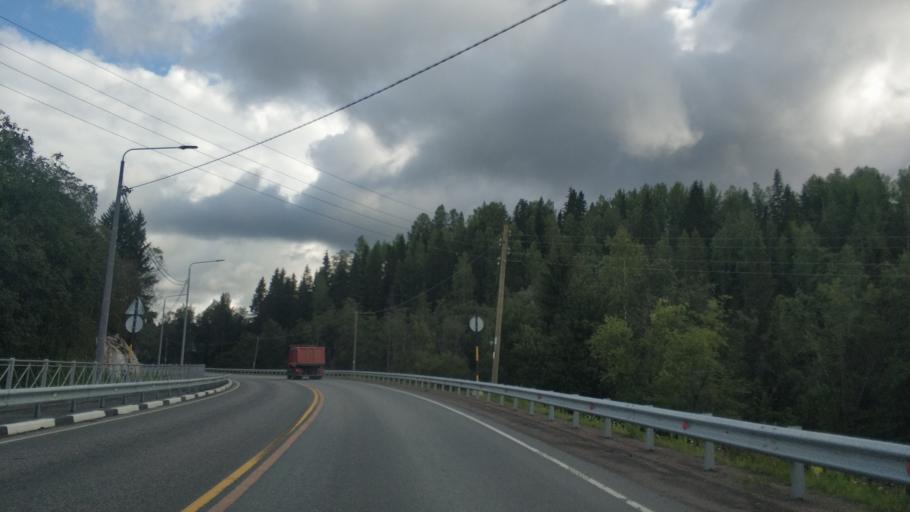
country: RU
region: Republic of Karelia
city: Ruskeala
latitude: 61.9382
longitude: 30.5912
